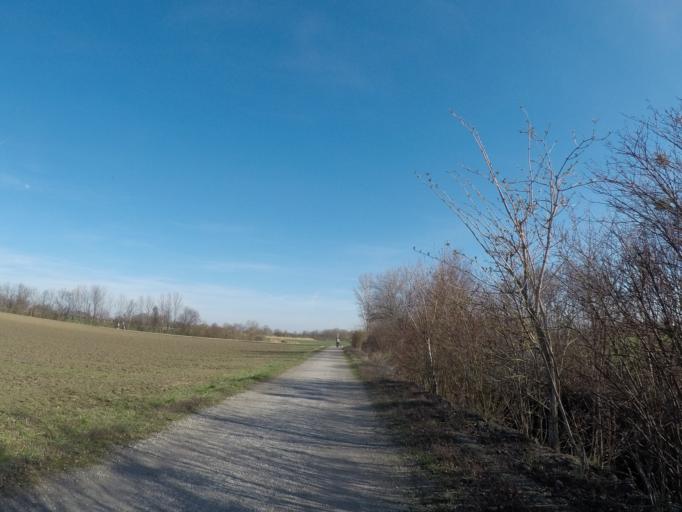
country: AT
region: Lower Austria
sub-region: Politischer Bezirk Modling
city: Biedermannsdorf
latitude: 48.0986
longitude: 16.3390
